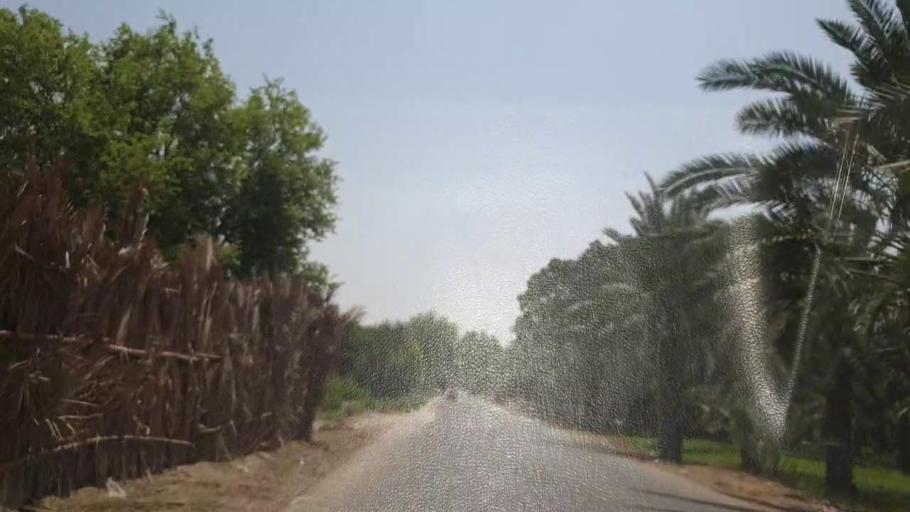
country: PK
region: Sindh
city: Kot Diji
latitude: 27.2826
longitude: 68.6357
